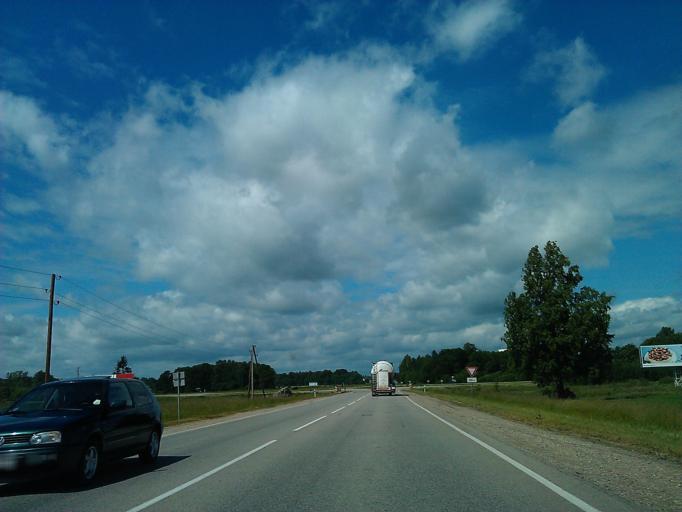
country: LV
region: Tukuma Rajons
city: Tukums
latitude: 56.9485
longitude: 23.1197
